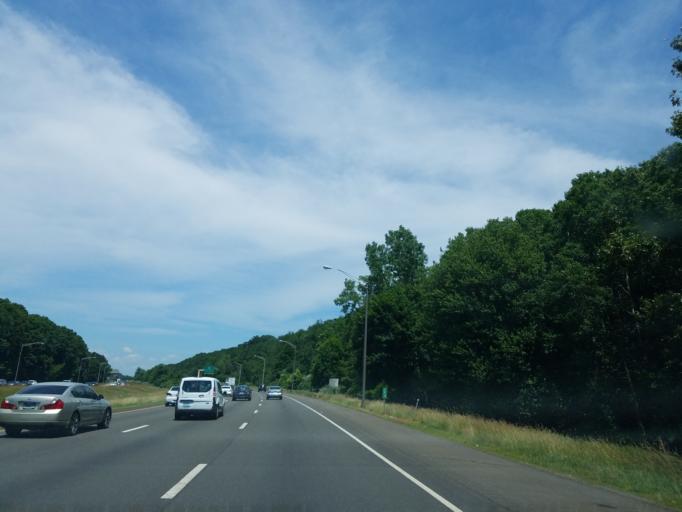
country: US
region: Connecticut
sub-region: New Haven County
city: North Haven
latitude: 41.4047
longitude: -72.8346
